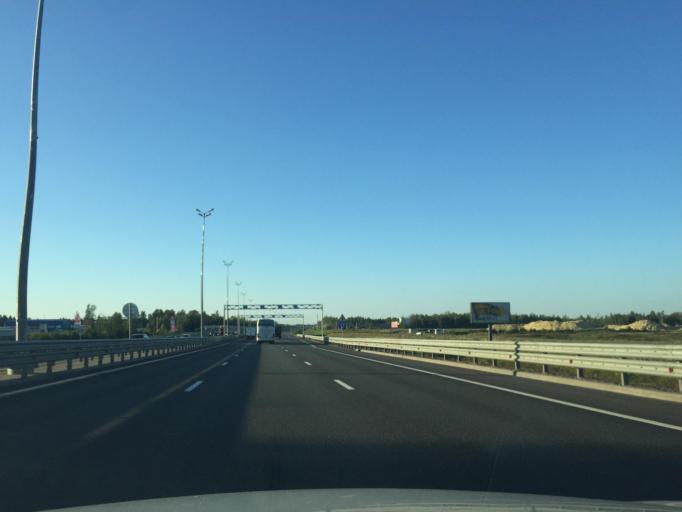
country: RU
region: Leningrad
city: Gatchina
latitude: 59.5575
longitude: 30.1660
